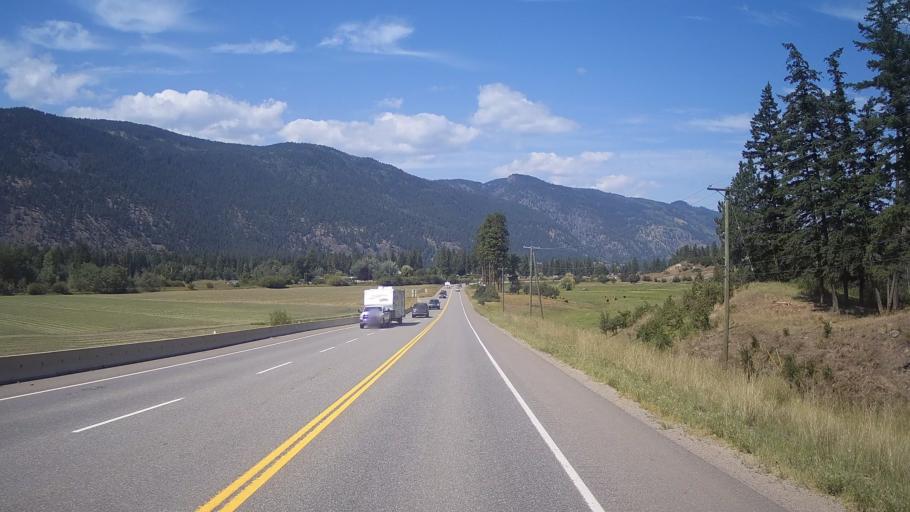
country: CA
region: British Columbia
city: Kamloops
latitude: 51.0198
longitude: -120.2229
